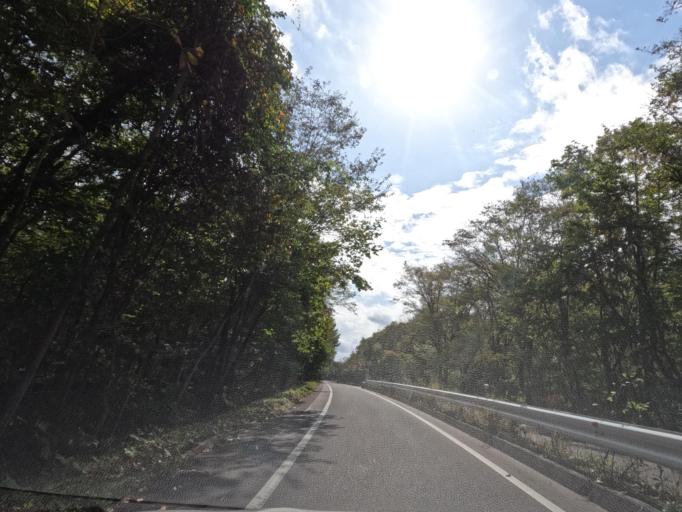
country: JP
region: Hokkaido
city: Chitose
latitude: 42.8005
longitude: 141.5683
